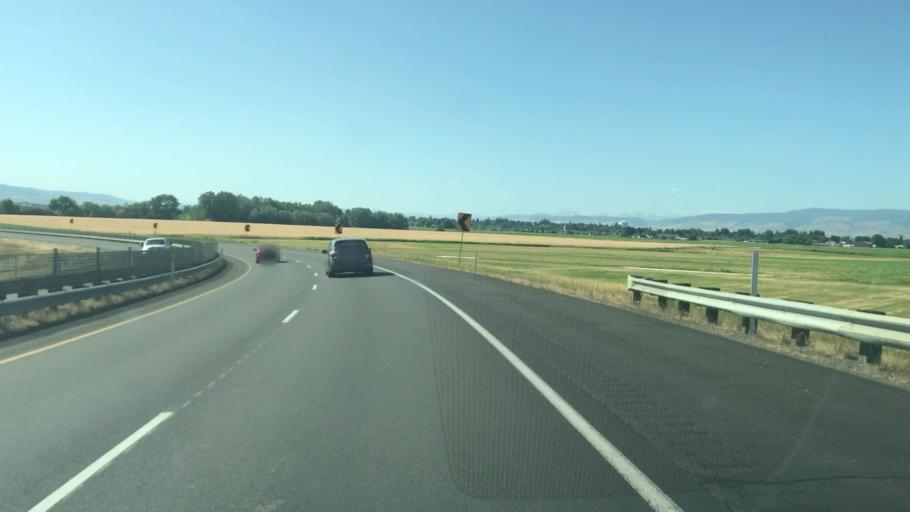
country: US
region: Washington
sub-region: Kittitas County
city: Ellensburg
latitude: 46.9720
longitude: -120.5118
